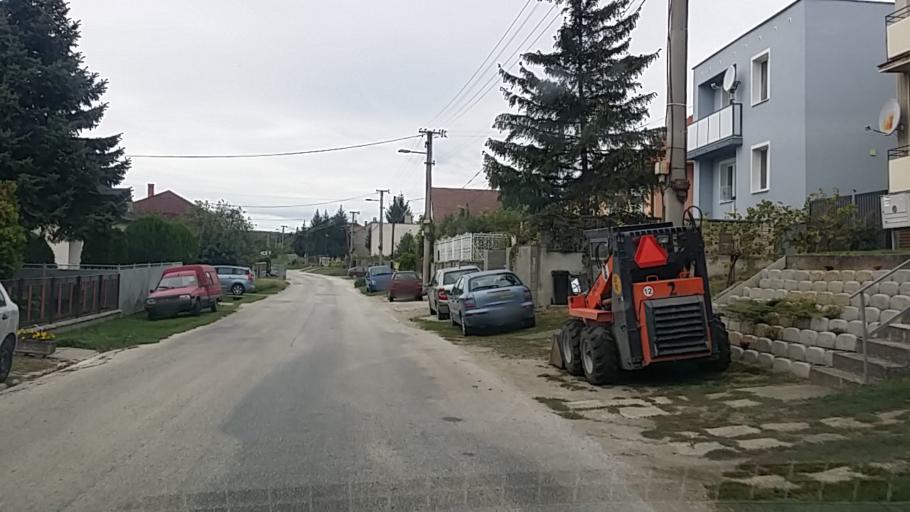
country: HU
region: Komarom-Esztergom
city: Esztergom
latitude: 47.8270
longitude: 18.7394
